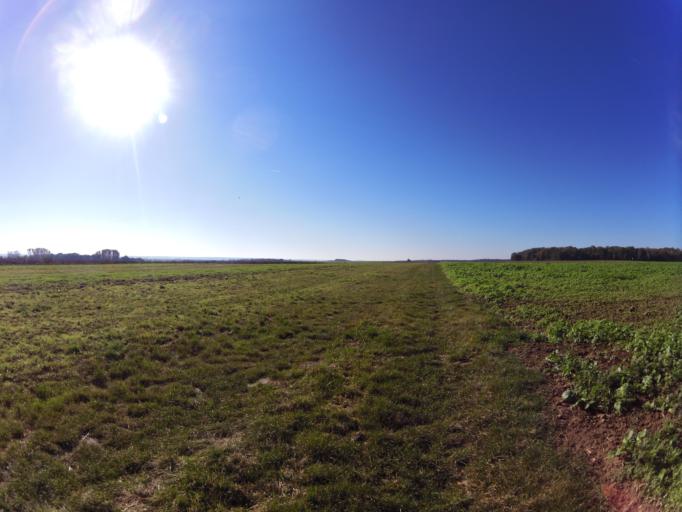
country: DE
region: Bavaria
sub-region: Regierungsbezirk Unterfranken
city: Geroldshausen
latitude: 49.6715
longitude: 9.9227
